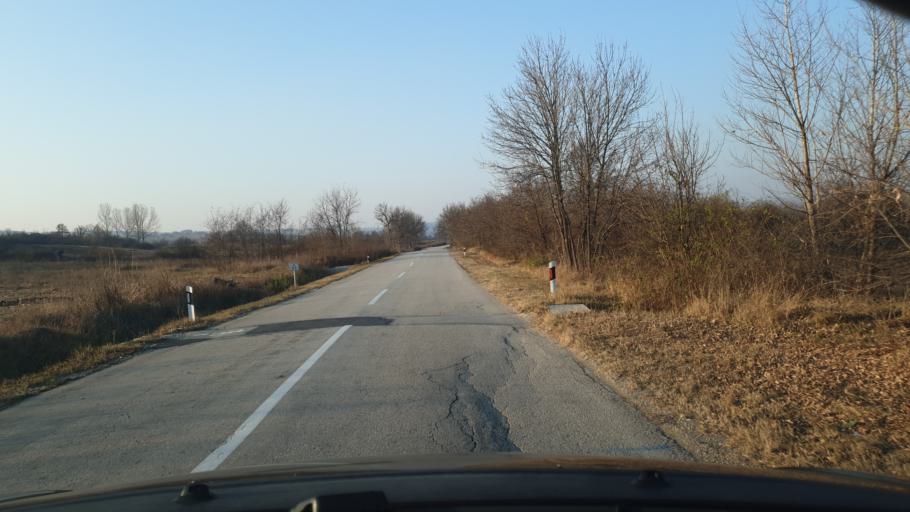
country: RS
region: Central Serbia
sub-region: Zajecarski Okrug
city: Zajecar
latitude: 43.9812
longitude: 22.2896
